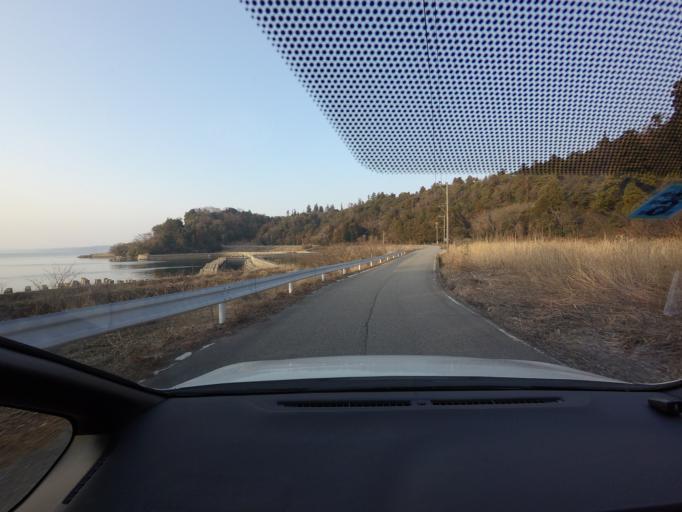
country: JP
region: Ishikawa
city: Nanao
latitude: 37.1467
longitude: 137.0240
